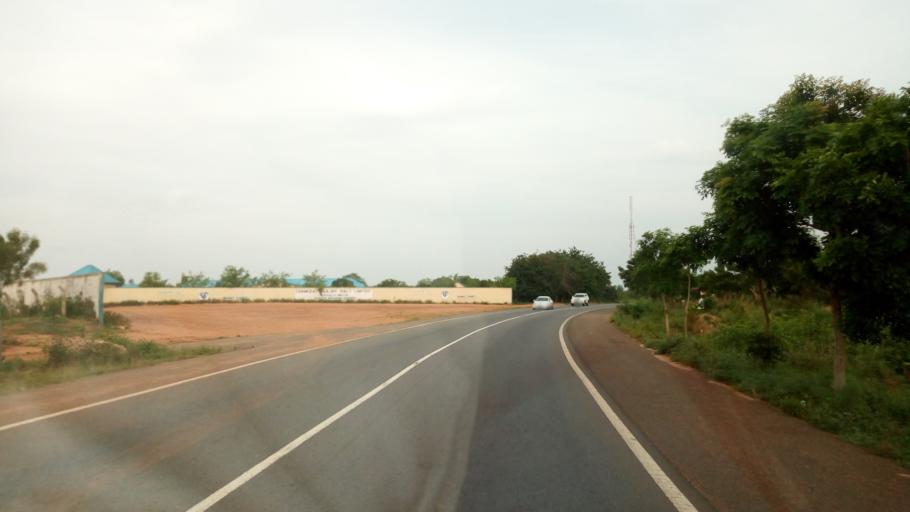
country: GH
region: Volta
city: Keta
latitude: 6.0512
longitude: 0.9713
